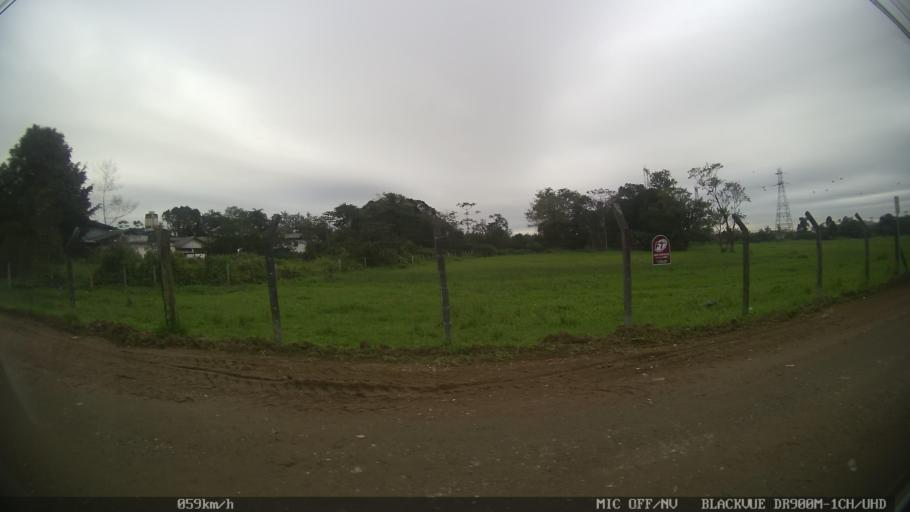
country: BR
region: Santa Catarina
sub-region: Joinville
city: Joinville
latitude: -26.2345
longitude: -48.8958
